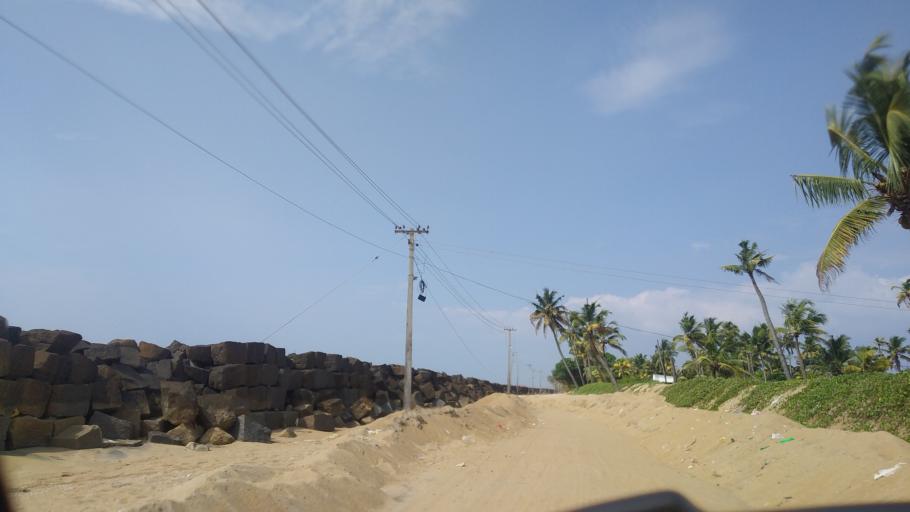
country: IN
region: Kerala
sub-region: Ernakulam
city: Elur
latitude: 10.0877
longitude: 76.1925
